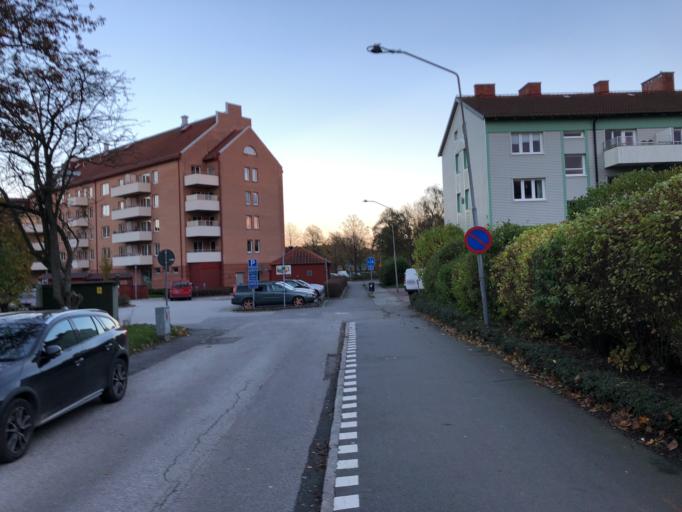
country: SE
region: Skane
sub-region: Svedala Kommun
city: Svedala
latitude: 55.5099
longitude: 13.2334
